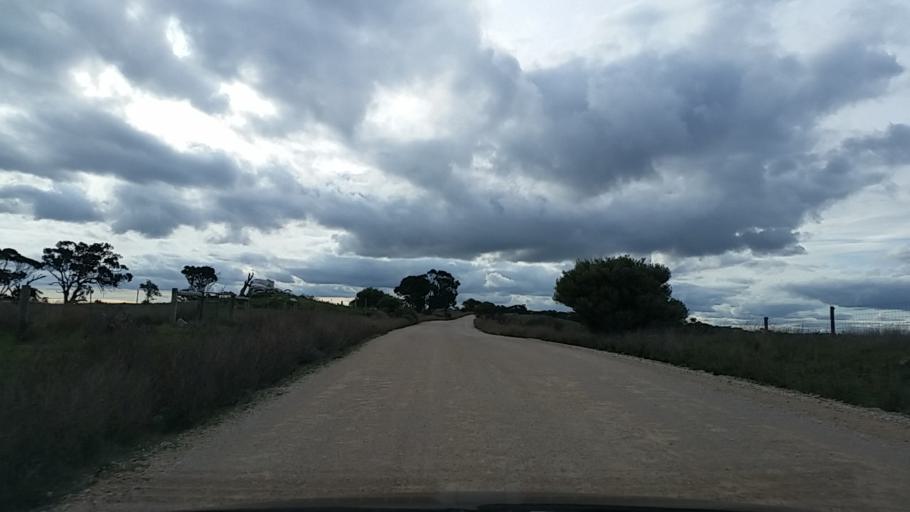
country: AU
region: South Australia
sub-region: Mount Barker
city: Callington
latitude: -35.0075
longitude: 139.0624
